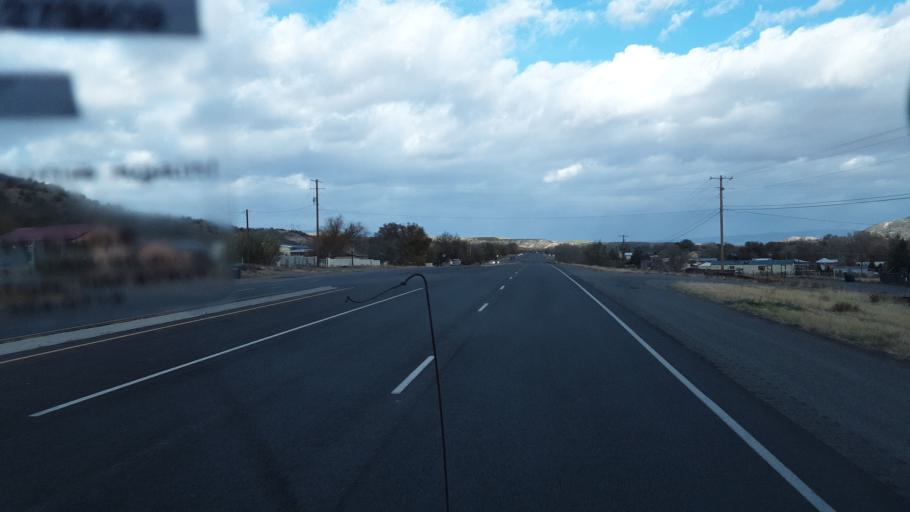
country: US
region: New Mexico
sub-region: Rio Arriba County
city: Ohkay Owingeh
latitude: 36.0387
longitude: -106.0983
